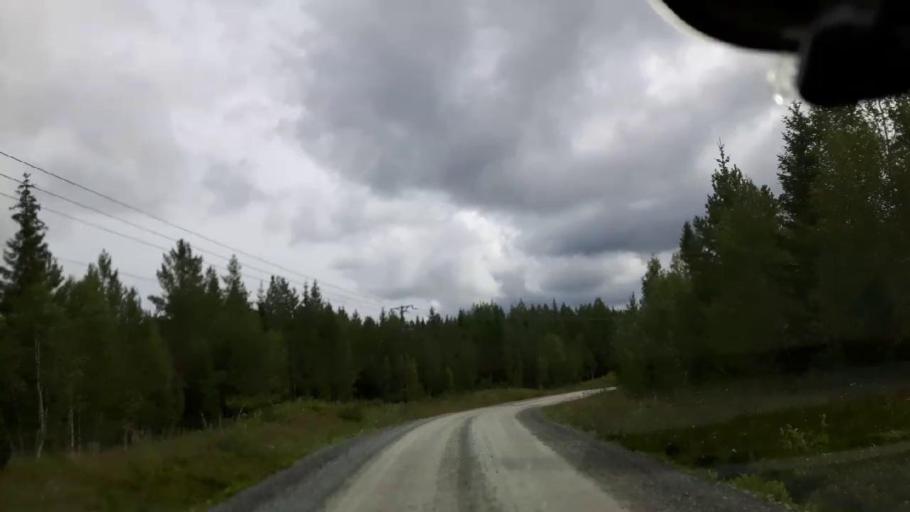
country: SE
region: Jaemtland
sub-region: Krokoms Kommun
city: Valla
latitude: 63.6042
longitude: 14.1305
